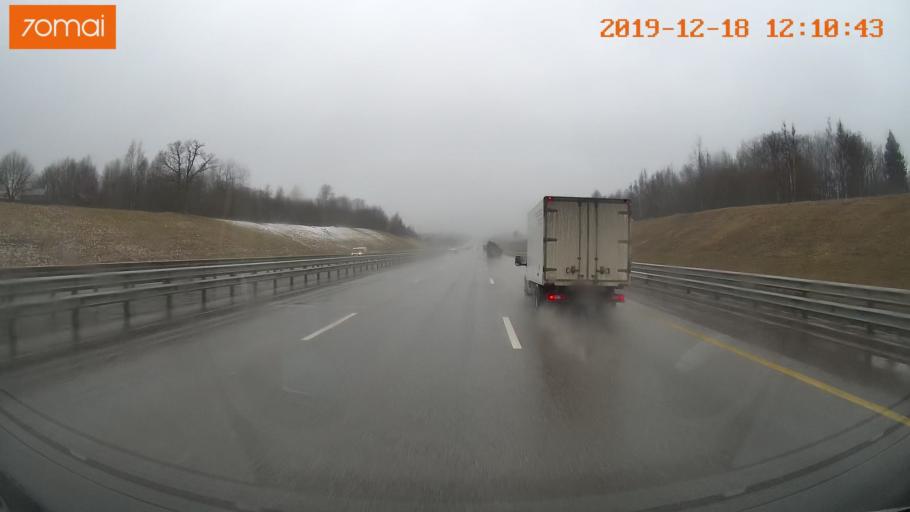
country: RU
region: Moskovskaya
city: Rumyantsevo
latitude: 55.9215
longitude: 36.5848
